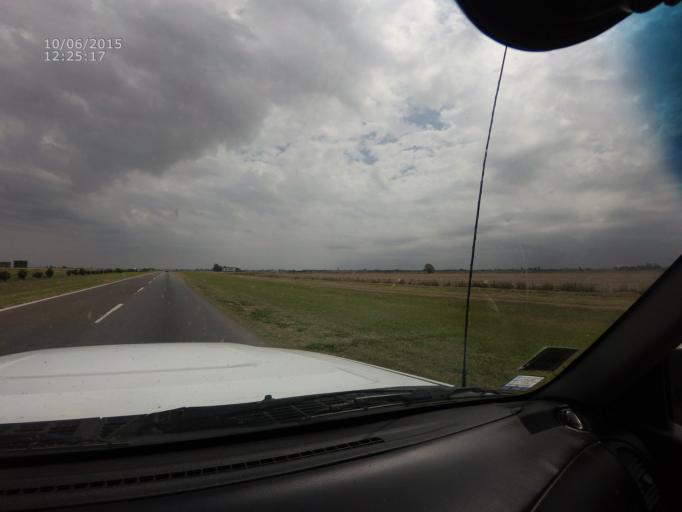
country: AR
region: Santa Fe
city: Roldan
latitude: -32.9074
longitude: -60.9948
